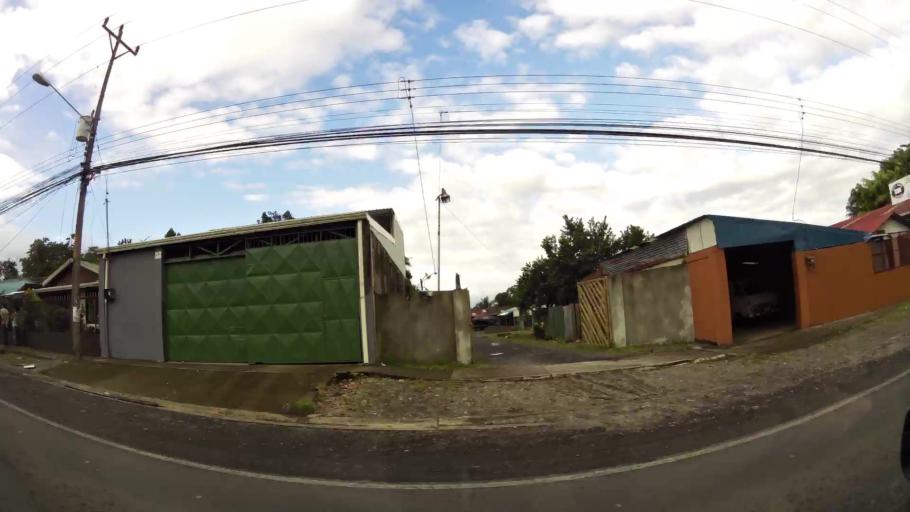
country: CR
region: Limon
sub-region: Canton de Pococi
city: Guapiles
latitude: 10.2046
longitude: -83.7960
